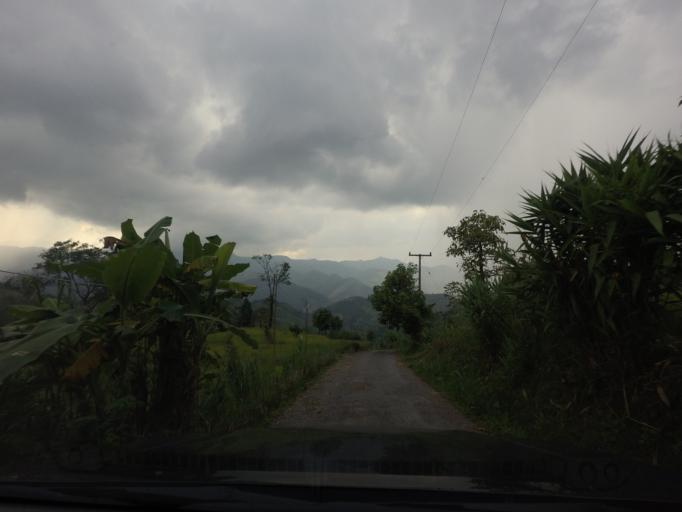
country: TH
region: Nan
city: Bo Kluea
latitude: 19.3505
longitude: 101.1784
